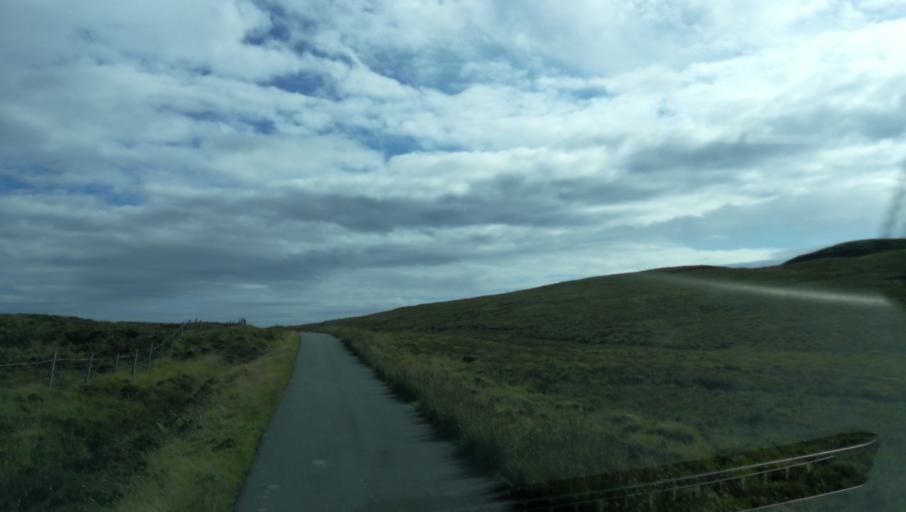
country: GB
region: Scotland
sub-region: Highland
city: Isle of Skye
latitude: 57.4127
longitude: -6.5665
